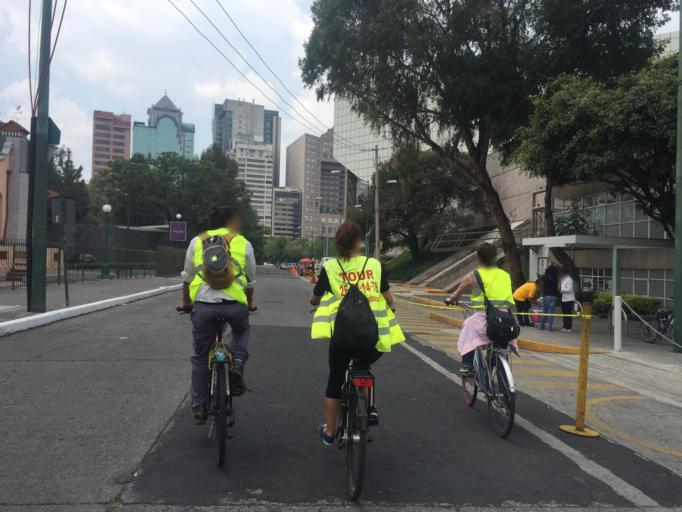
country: MX
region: Mexico City
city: Polanco
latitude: 19.4239
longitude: -99.1958
